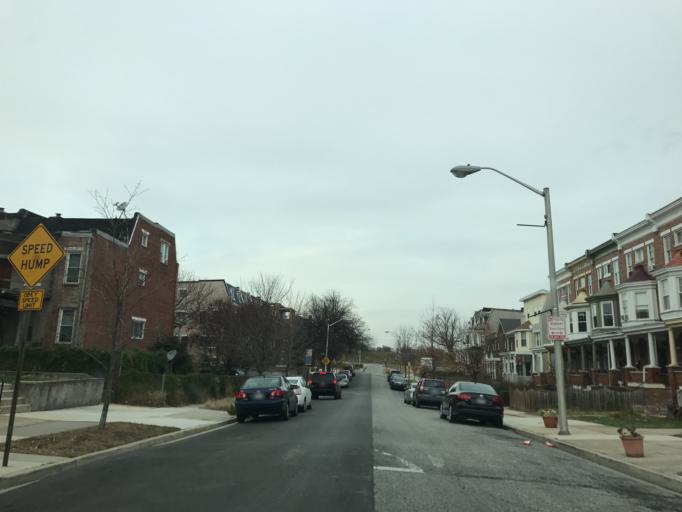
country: US
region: Maryland
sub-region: City of Baltimore
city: Baltimore
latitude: 39.3154
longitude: -76.6339
